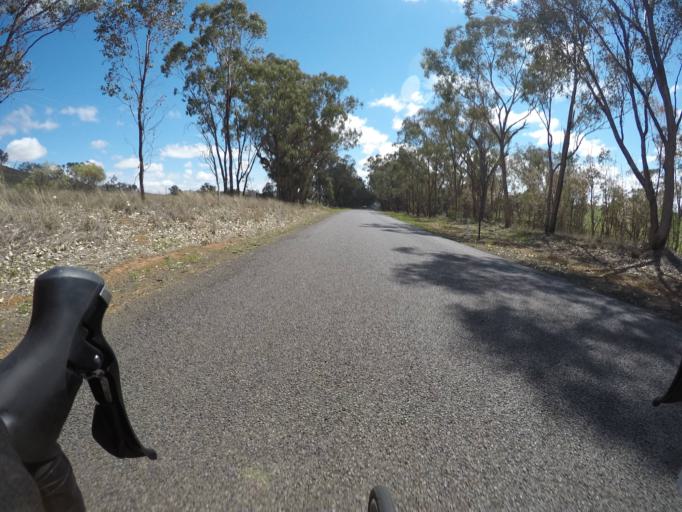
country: AU
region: New South Wales
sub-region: Dubbo Municipality
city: Dubbo
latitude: -32.5384
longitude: 148.5475
